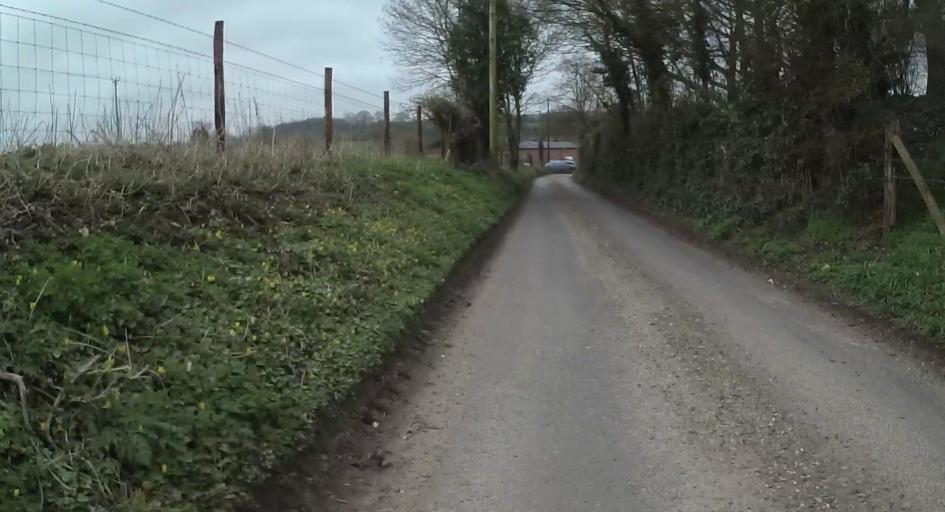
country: GB
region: England
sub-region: Hampshire
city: Four Marks
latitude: 51.1068
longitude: -1.1277
